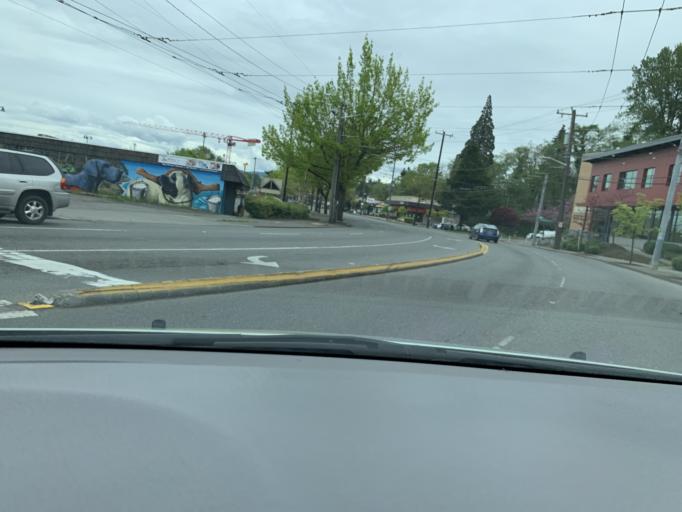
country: US
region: Washington
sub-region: King County
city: Bryn Mawr-Skyway
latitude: 47.5200
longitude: -122.2697
